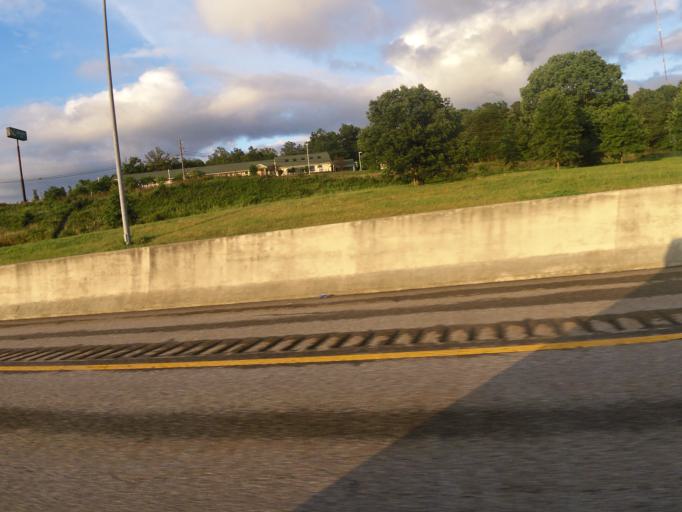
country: US
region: Kentucky
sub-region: Laurel County
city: London
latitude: 37.1478
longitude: -84.1115
